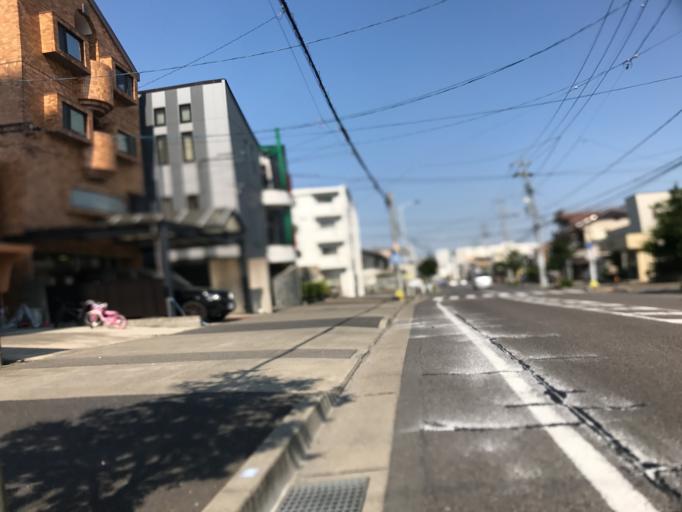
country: JP
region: Aichi
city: Nagoya-shi
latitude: 35.1752
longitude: 136.9308
